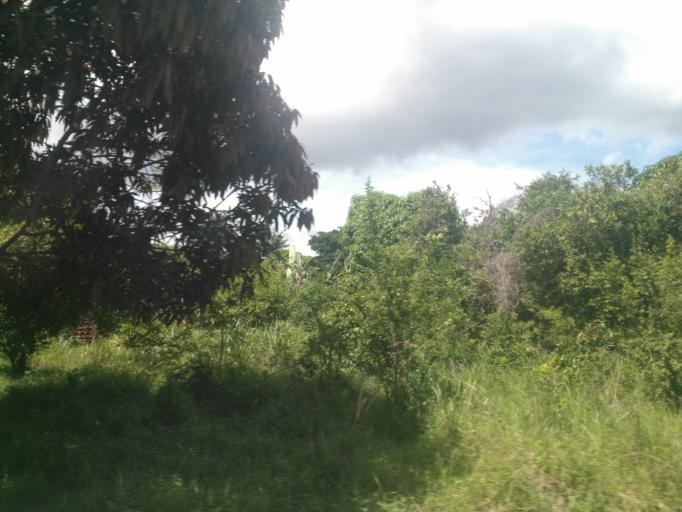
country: TZ
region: Zanzibar North
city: Gamba
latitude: -5.9346
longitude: 39.3413
